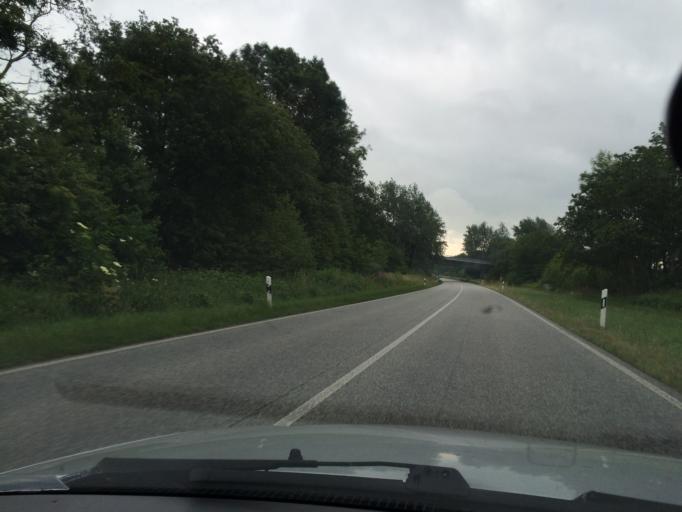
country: DE
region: Schleswig-Holstein
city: Sieverstedt
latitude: 54.6488
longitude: 9.4488
